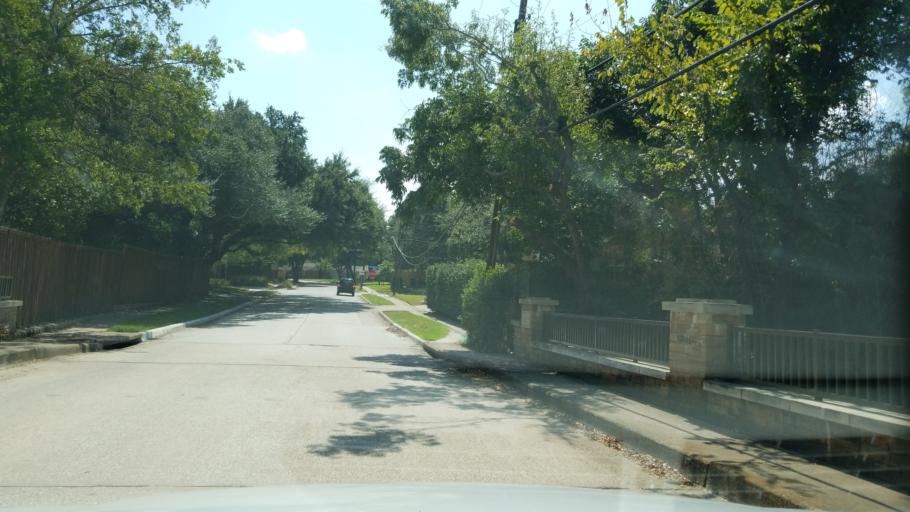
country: US
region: Texas
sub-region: Dallas County
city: Richardson
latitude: 32.9568
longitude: -96.7495
